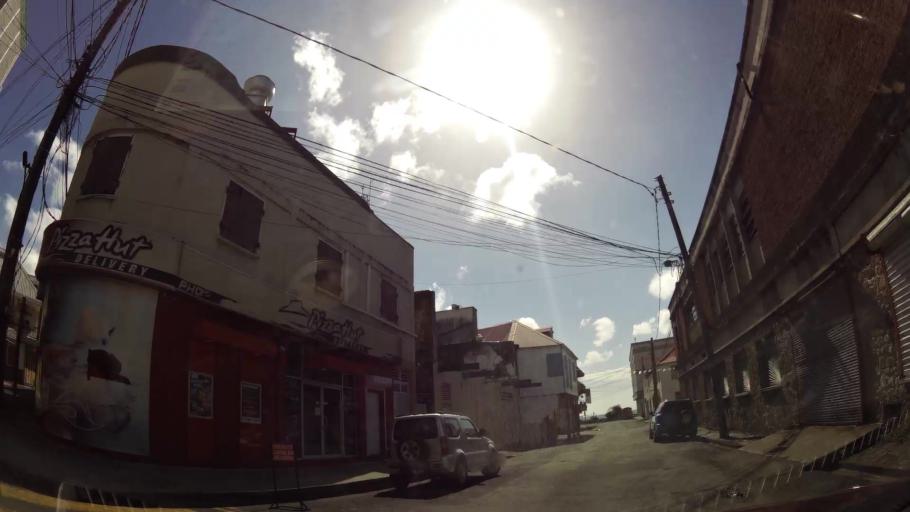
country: DM
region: Saint George
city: Roseau
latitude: 15.2979
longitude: -61.3877
